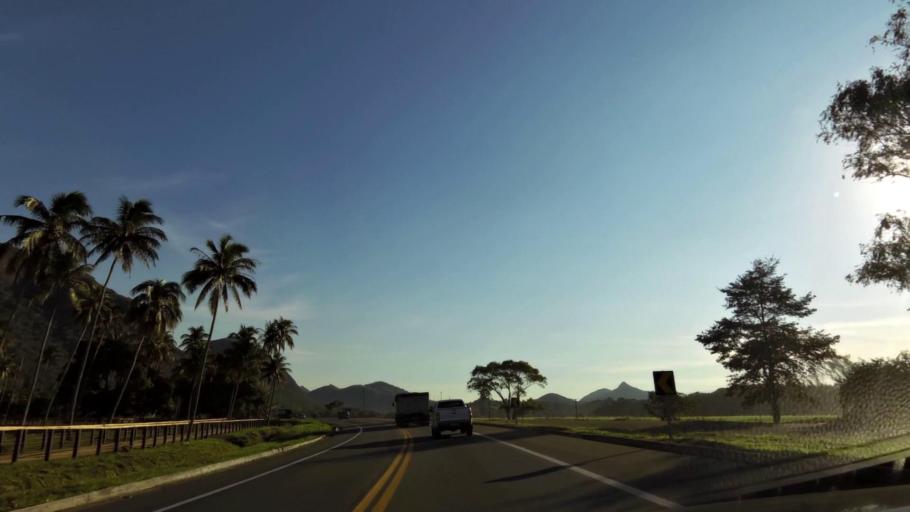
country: BR
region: Espirito Santo
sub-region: Guarapari
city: Guarapari
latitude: -20.6033
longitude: -40.5027
